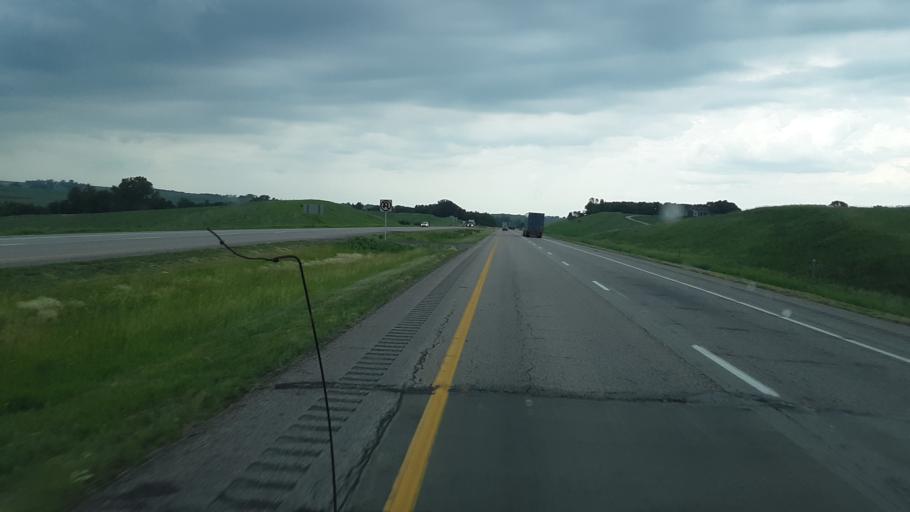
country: US
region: Iowa
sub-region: Pottawattamie County
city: Council Bluffs
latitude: 41.3873
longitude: -95.6683
